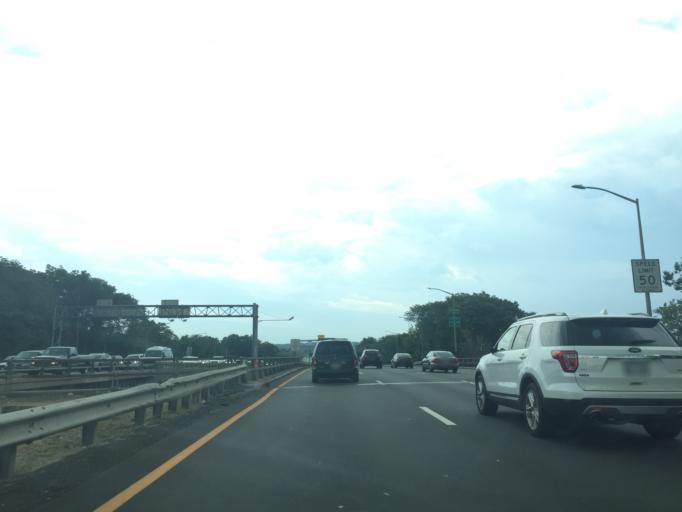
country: US
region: New York
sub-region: Richmond County
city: Bloomfield
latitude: 40.6152
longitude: -74.1578
